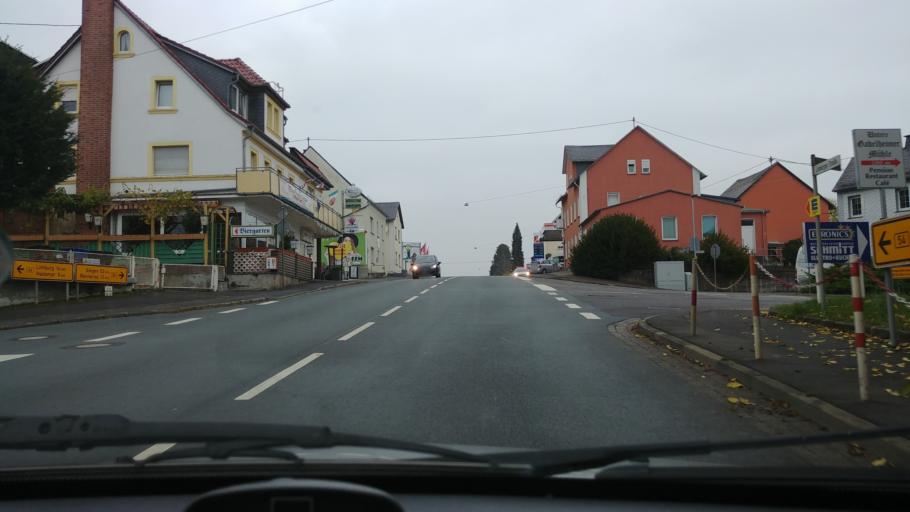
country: DE
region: Hesse
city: Waldbrunn
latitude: 50.5046
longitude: 8.0650
